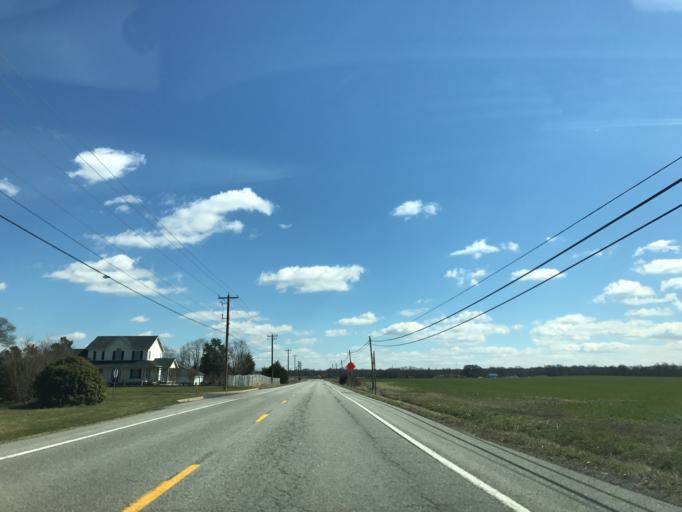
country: US
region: Maryland
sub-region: Queen Anne's County
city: Centreville
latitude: 39.0304
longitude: -76.0407
